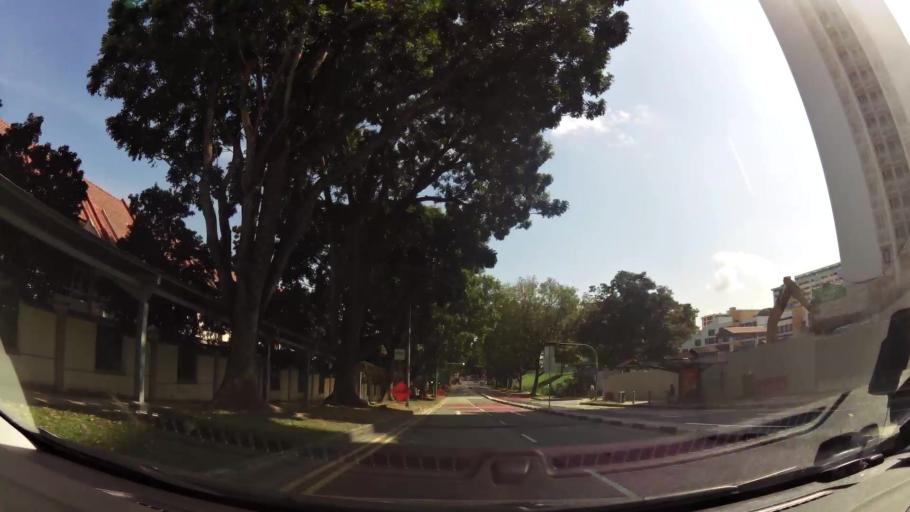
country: SG
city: Singapore
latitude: 1.3763
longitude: 103.8342
